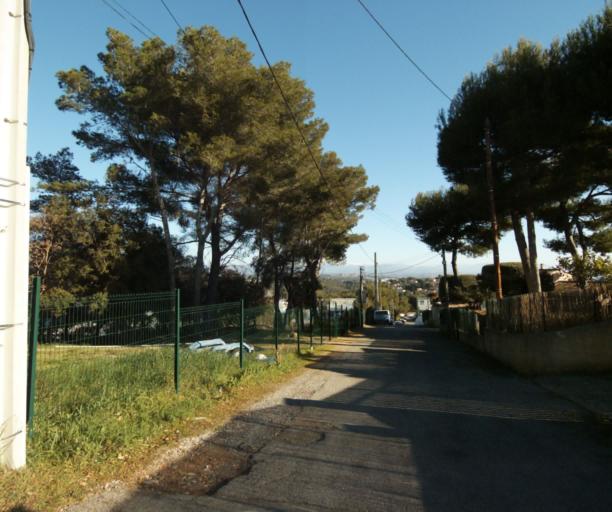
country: FR
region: Provence-Alpes-Cote d'Azur
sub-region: Departement des Alpes-Maritimes
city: Vallauris
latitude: 43.5998
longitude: 7.0777
